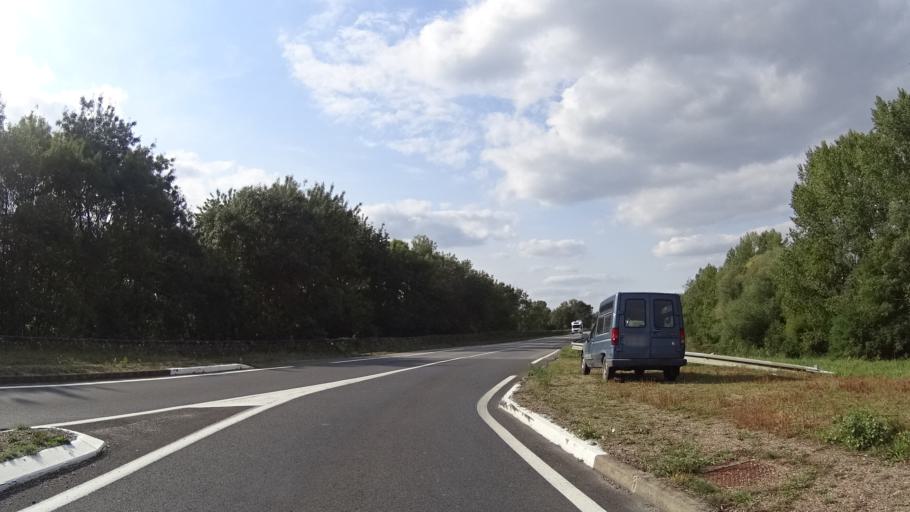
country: FR
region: Pays de la Loire
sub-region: Departement de Maine-et-Loire
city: Saint-Martin-de-la-Place
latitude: 47.3064
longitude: -0.1339
